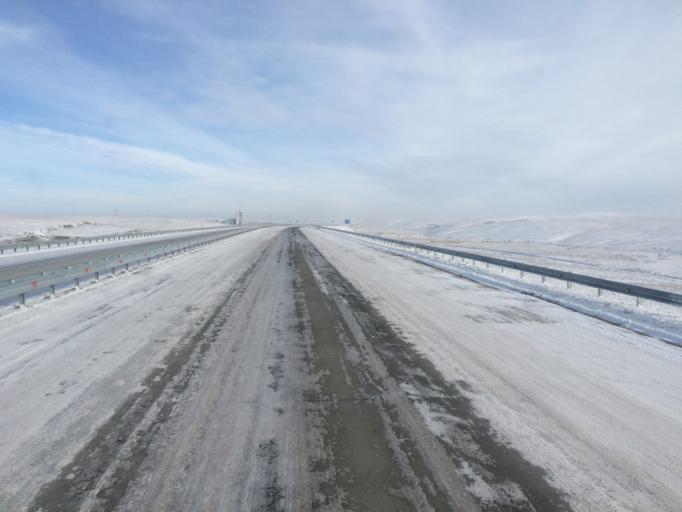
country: KZ
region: Zhambyl
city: Georgiyevka
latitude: 43.3527
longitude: 74.5583
